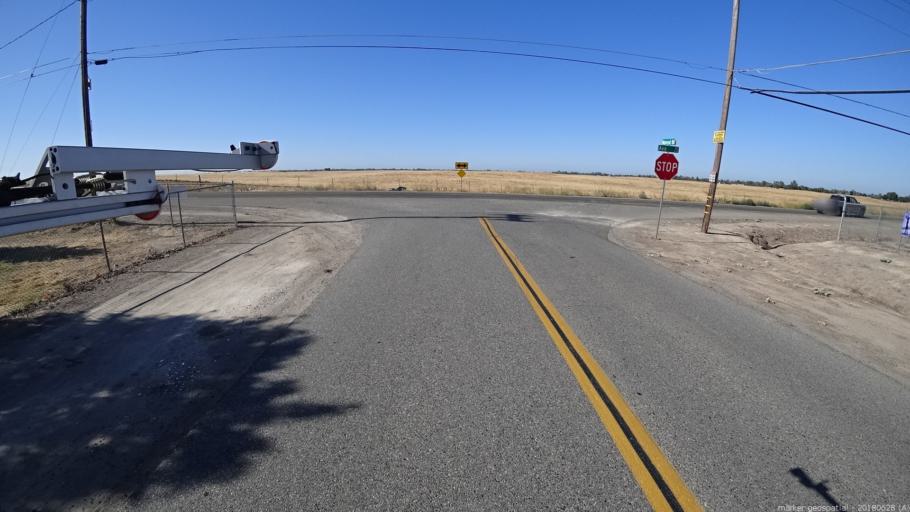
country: US
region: California
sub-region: Madera County
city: Bonadelle Ranchos-Madera Ranchos
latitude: 36.9669
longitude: -119.8853
